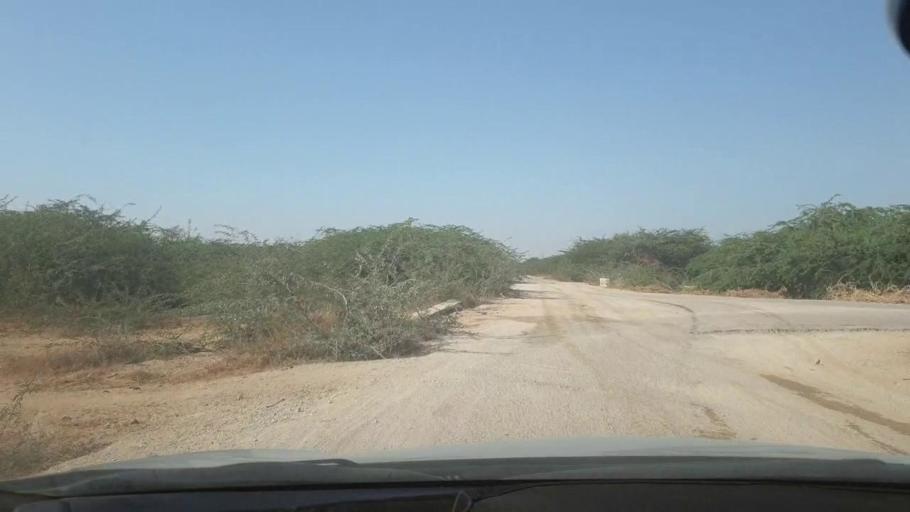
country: PK
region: Sindh
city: Malir Cantonment
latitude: 25.1484
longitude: 67.1651
